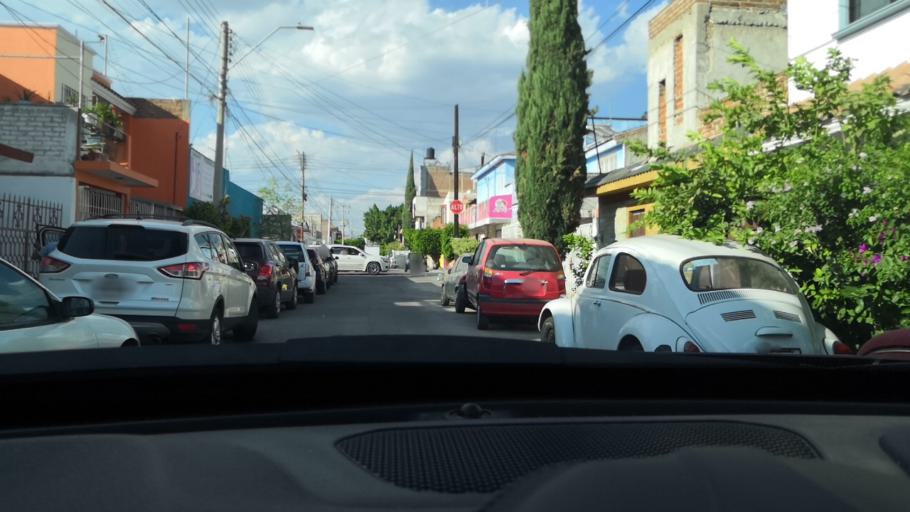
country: MX
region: Guanajuato
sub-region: Leon
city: San Jose de Duran (Los Troncoso)
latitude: 21.0940
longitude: -101.6520
